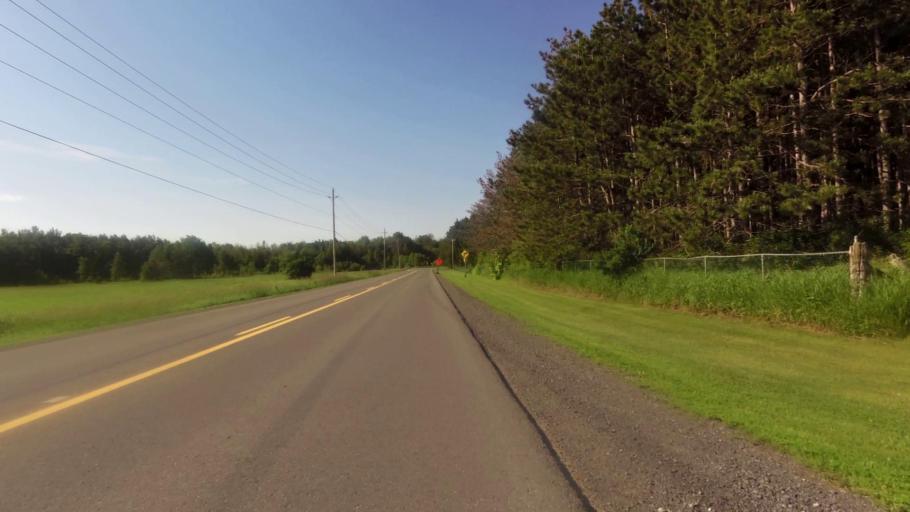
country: CA
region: Ontario
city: Ottawa
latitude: 45.2241
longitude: -75.5609
